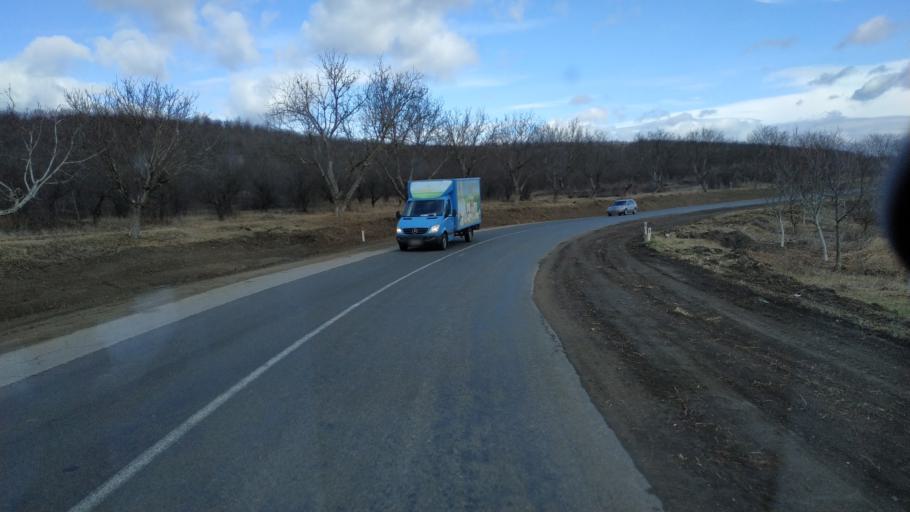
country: MD
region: Stinga Nistrului
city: Bucovat
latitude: 47.1690
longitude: 28.4408
